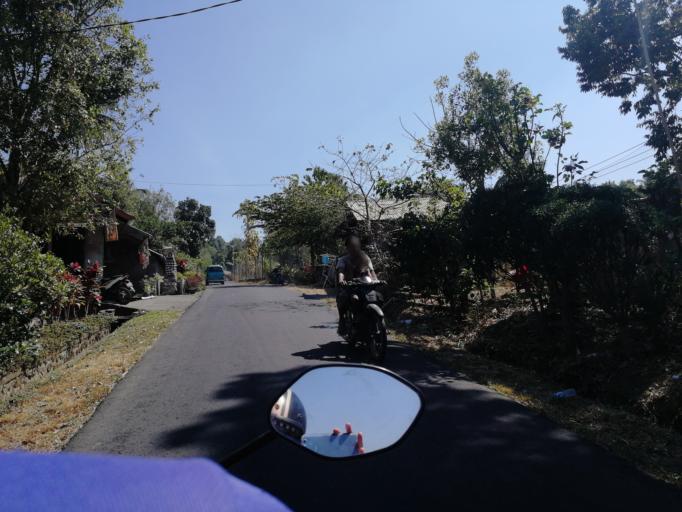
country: ID
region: Bali
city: Banjar Kedisan
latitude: -8.1572
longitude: 115.3065
